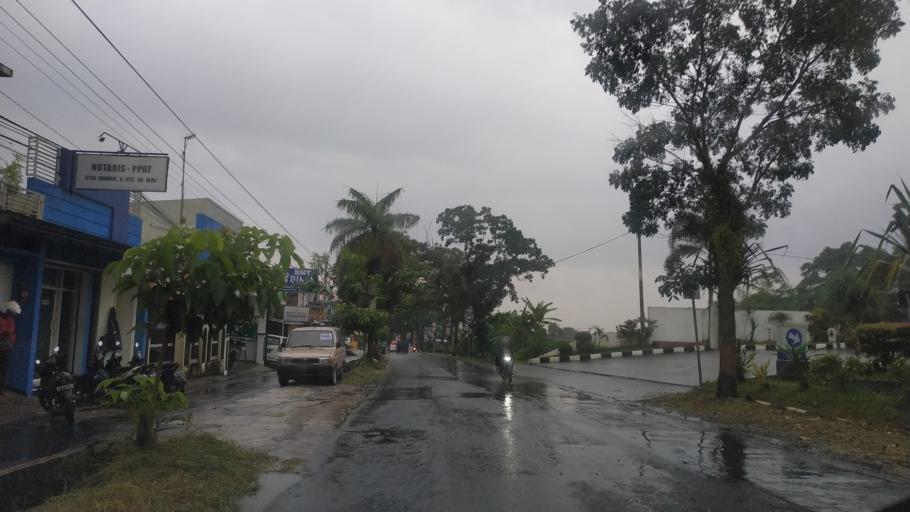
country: ID
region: Central Java
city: Magelang
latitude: -7.3138
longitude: 110.1647
